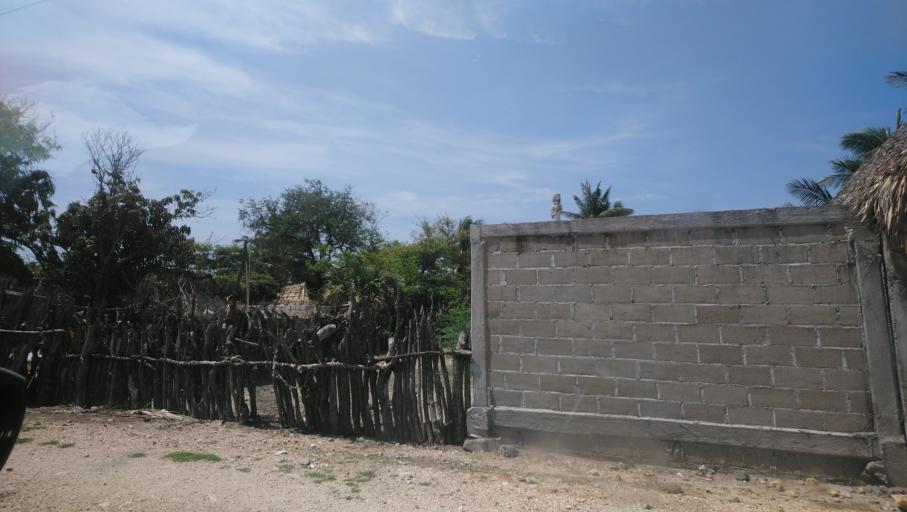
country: MX
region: Oaxaca
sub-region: Salina Cruz
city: Salina Cruz
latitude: 16.1906
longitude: -95.1176
